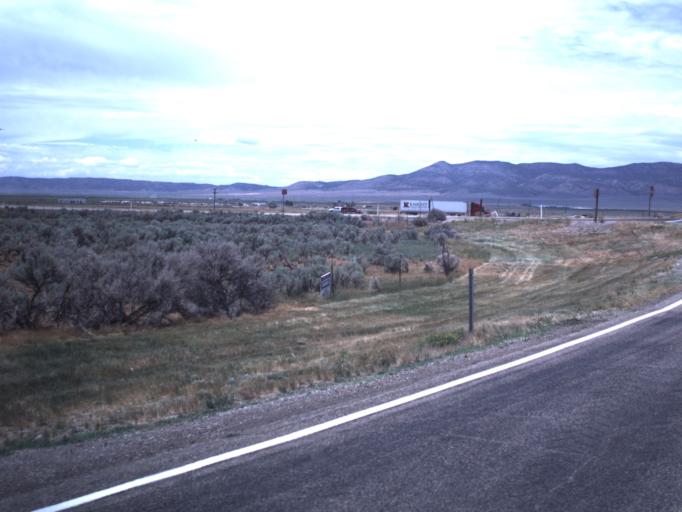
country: US
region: Utah
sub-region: Iron County
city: Parowan
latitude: 37.9073
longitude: -112.7752
